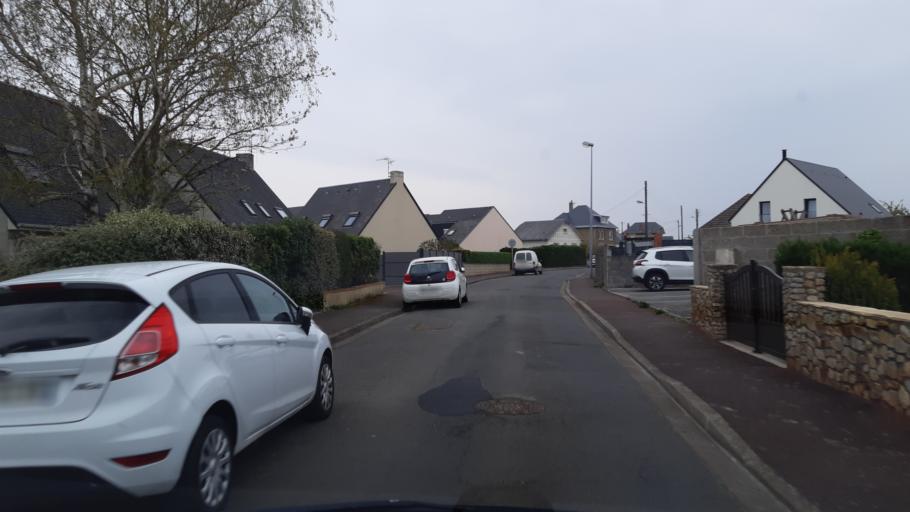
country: FR
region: Lower Normandy
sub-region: Departement de la Manche
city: Donville-les-Bains
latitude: 48.8387
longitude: -1.5793
